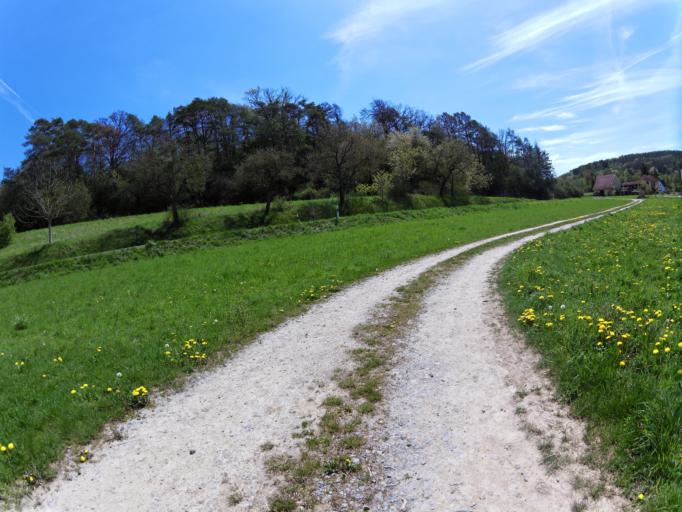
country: DE
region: Bavaria
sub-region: Regierungsbezirk Unterfranken
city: Greussenheim
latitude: 49.8156
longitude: 9.7705
